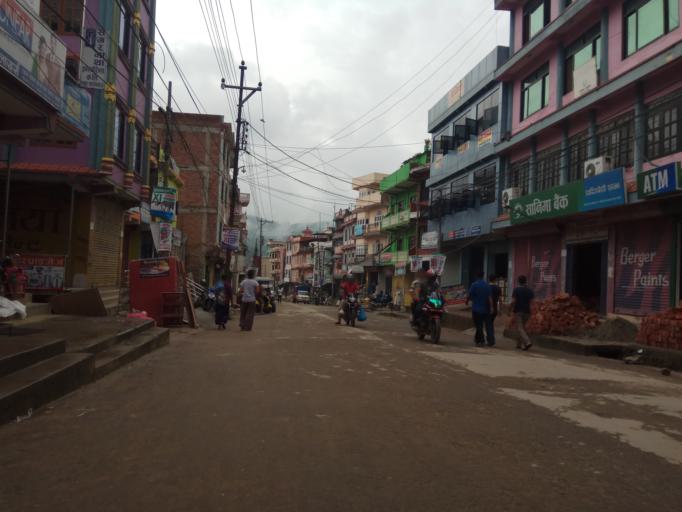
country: NP
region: Central Region
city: Kirtipur
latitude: 27.9114
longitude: 84.8919
